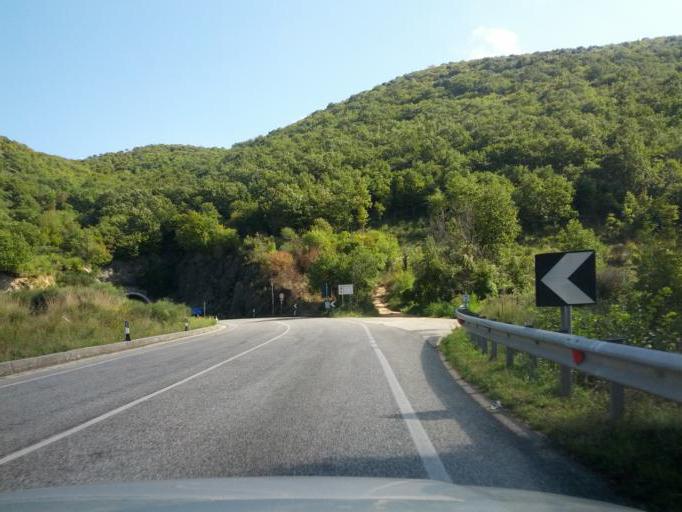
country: IT
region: Campania
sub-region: Provincia di Caserta
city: Mignano Monte Lungo
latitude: 41.4417
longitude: 14.0005
